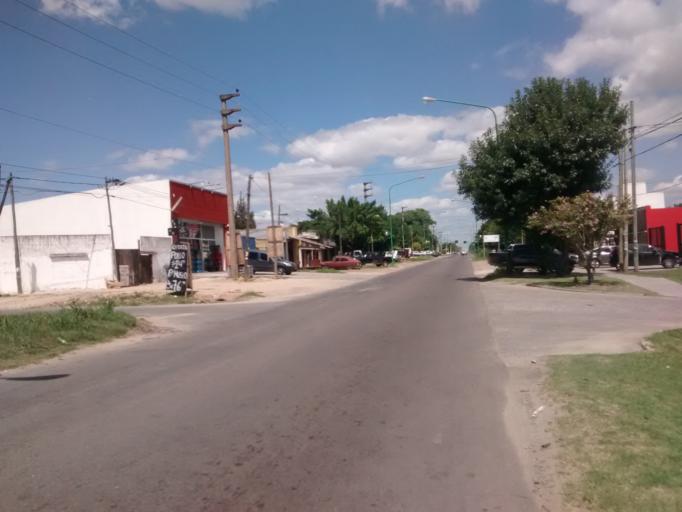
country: AR
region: Buenos Aires
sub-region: Partido de La Plata
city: La Plata
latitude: -34.9273
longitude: -58.0027
